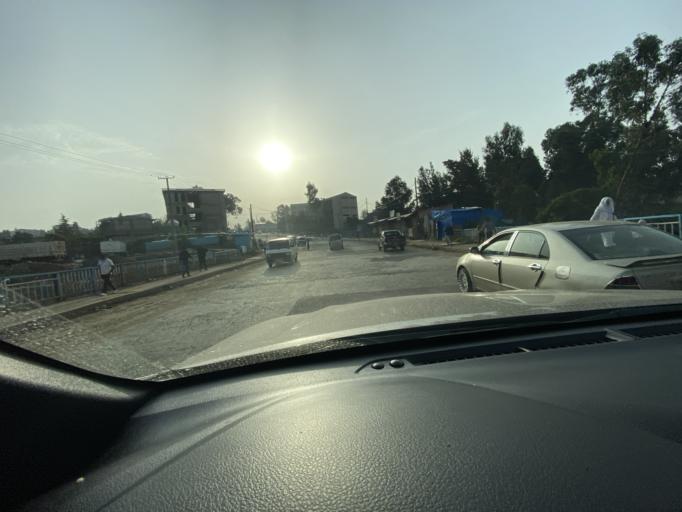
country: ET
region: Adis Abeba
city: Addis Ababa
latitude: 9.0217
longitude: 38.7190
